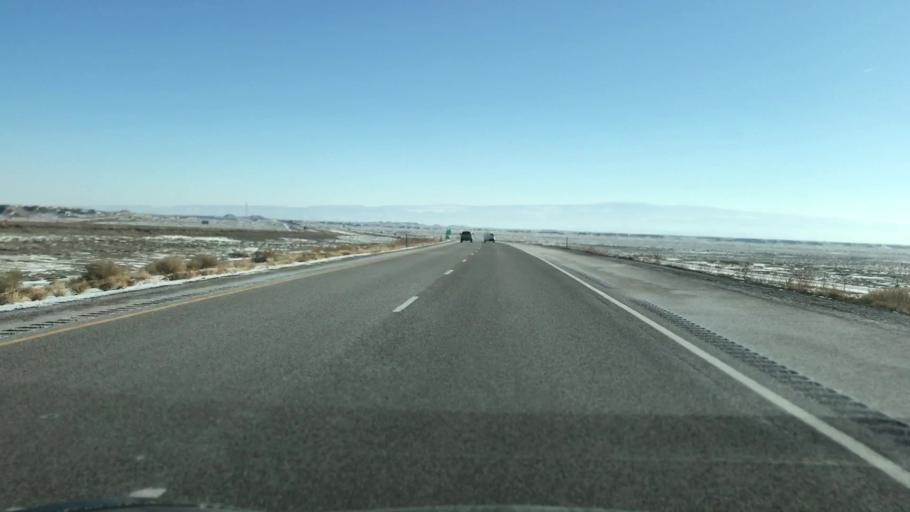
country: US
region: Utah
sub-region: Grand County
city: Moab
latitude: 38.9322
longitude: -109.4366
